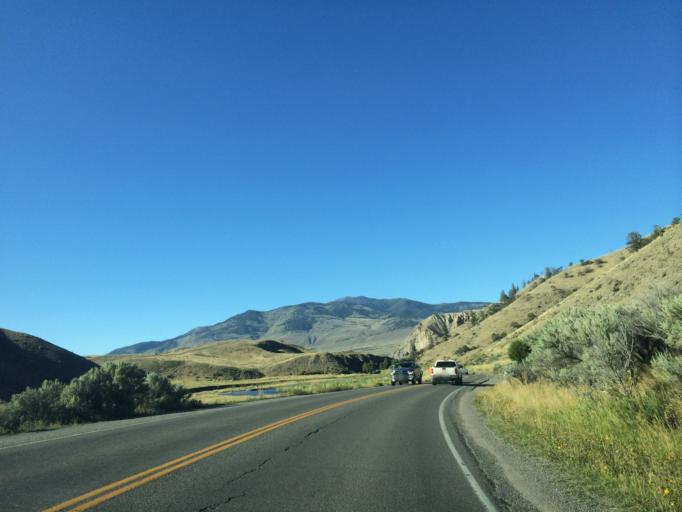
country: US
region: Montana
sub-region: Gallatin County
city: West Yellowstone
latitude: 44.9945
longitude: -110.6936
